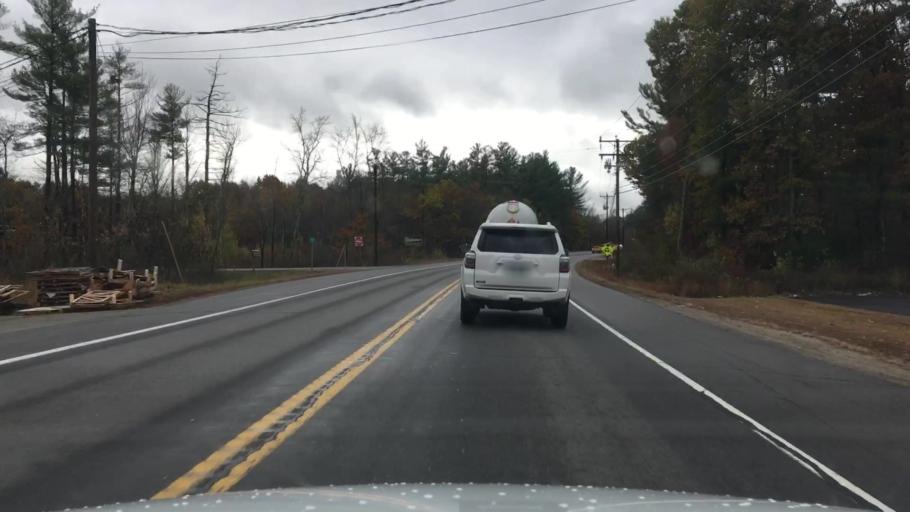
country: US
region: New Hampshire
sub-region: Strafford County
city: Lee
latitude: 43.1454
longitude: -71.0080
